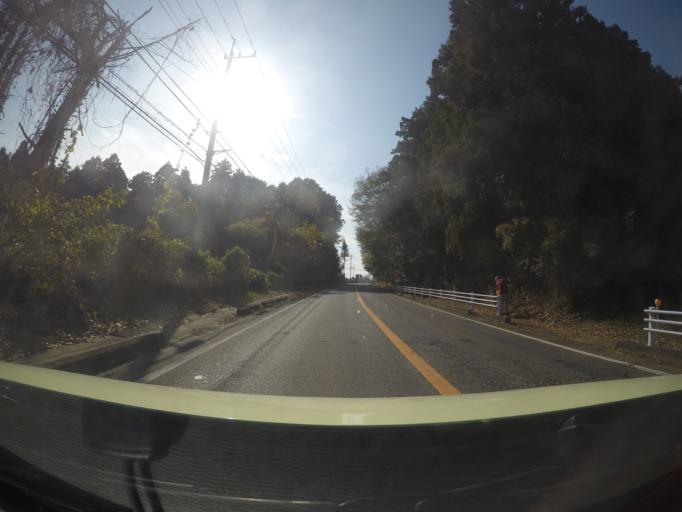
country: JP
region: Ibaraki
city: Tsukuba
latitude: 36.1223
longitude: 140.1160
